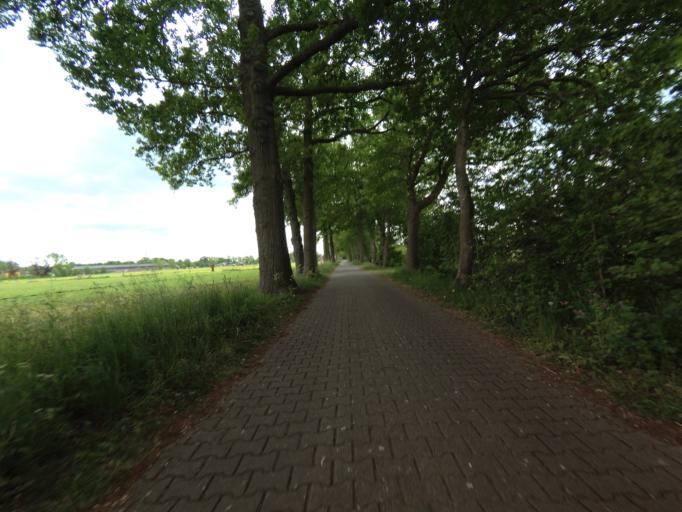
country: NL
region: Utrecht
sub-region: Gemeente Leusden
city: Leusden
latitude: 52.1556
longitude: 5.4393
